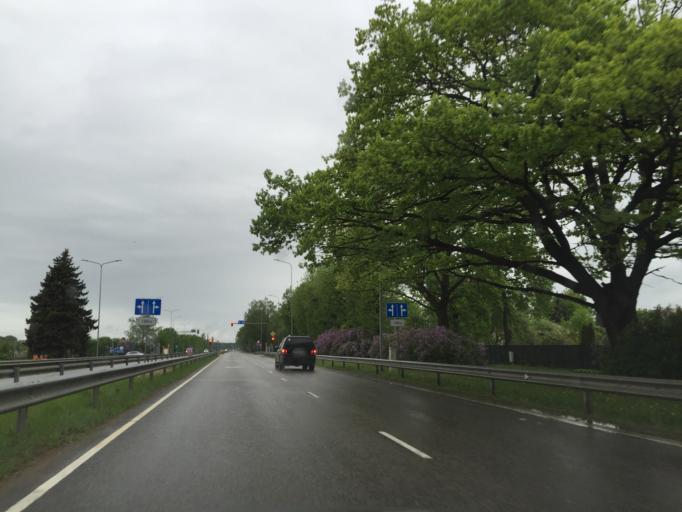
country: LV
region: Ogre
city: Ogre
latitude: 56.7982
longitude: 24.6224
